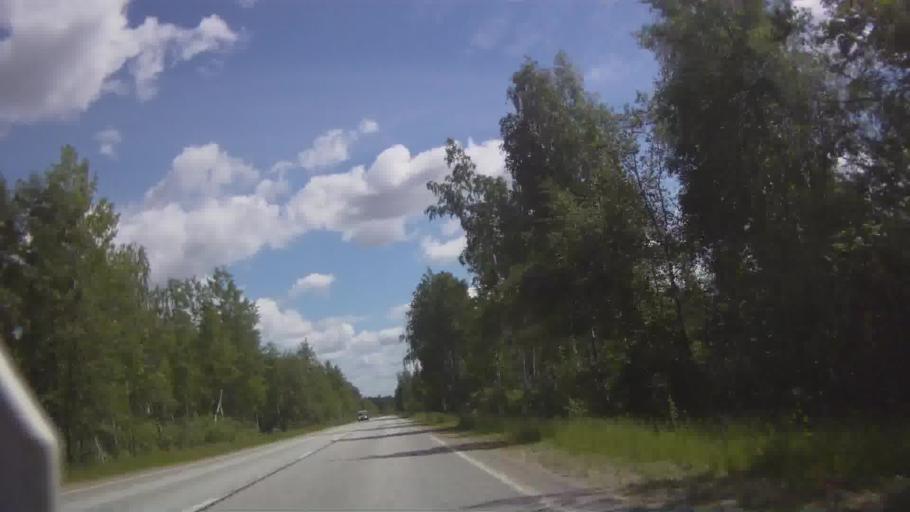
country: LV
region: Livani
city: Livani
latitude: 56.5292
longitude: 26.3770
